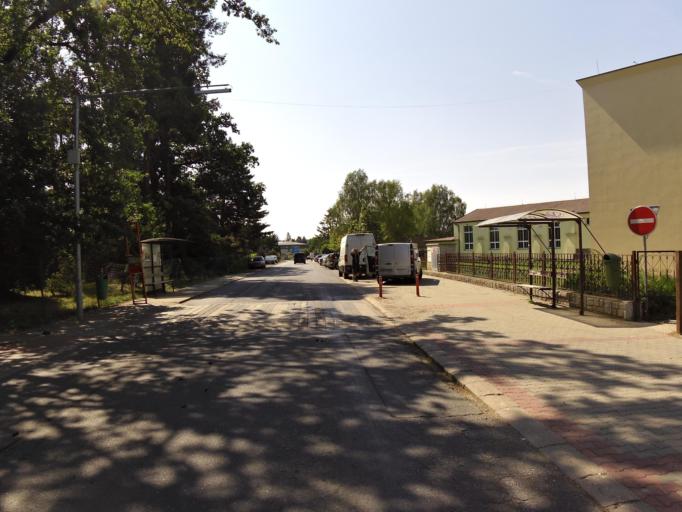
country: CZ
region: Central Bohemia
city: Mukarov
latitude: 49.9923
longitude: 14.7440
